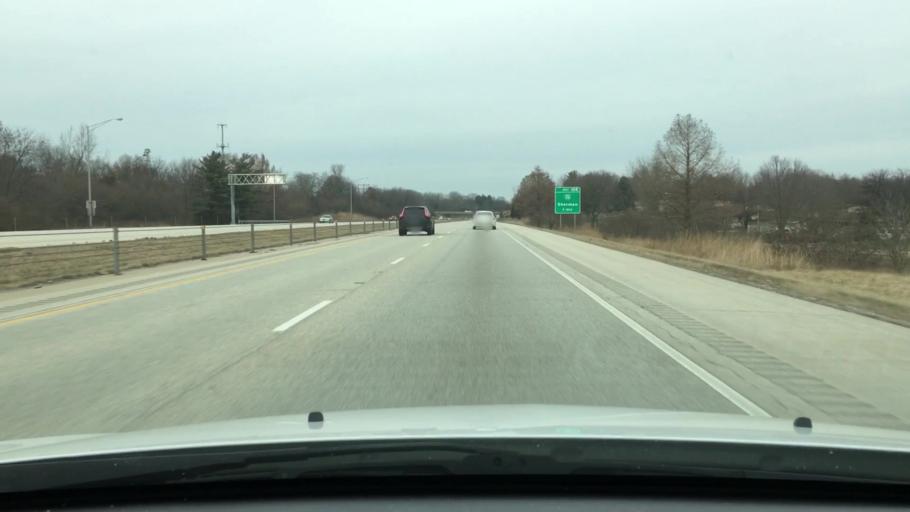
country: US
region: Illinois
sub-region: Sangamon County
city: Sherman
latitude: 39.8886
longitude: -89.5958
